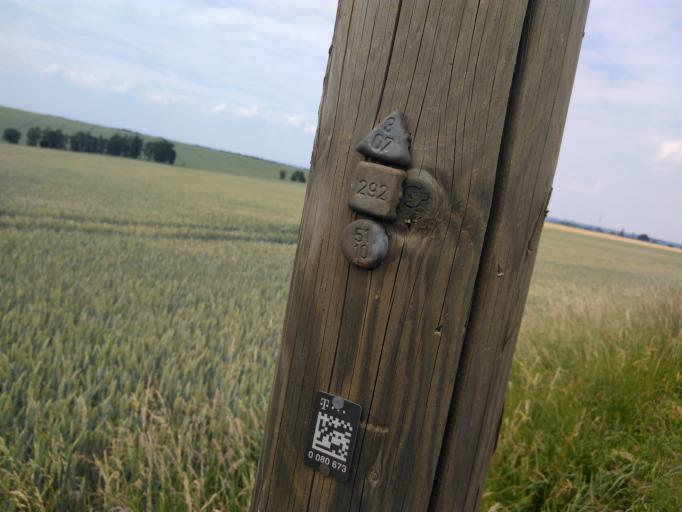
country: DE
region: Thuringia
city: Gosen
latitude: 51.0068
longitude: 11.8734
